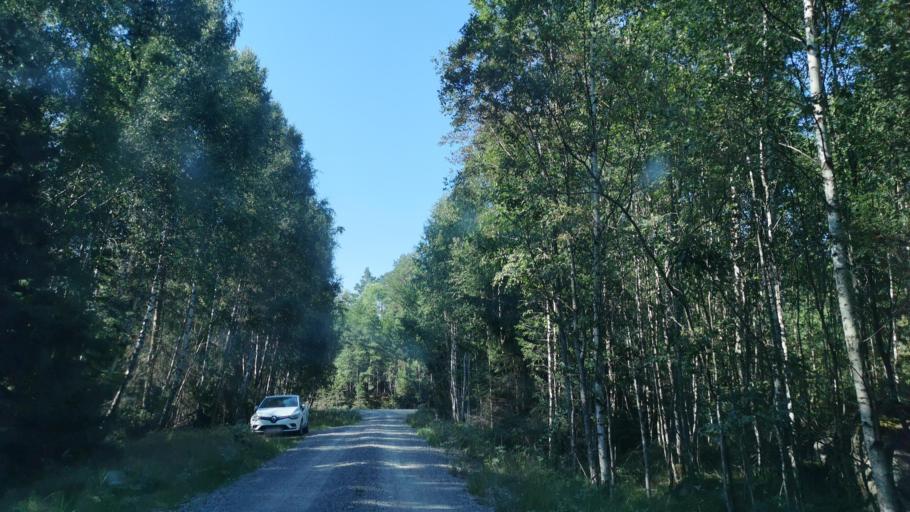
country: SE
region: OEstergoetland
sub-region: Norrkopings Kommun
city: Jursla
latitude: 58.7099
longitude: 16.1855
